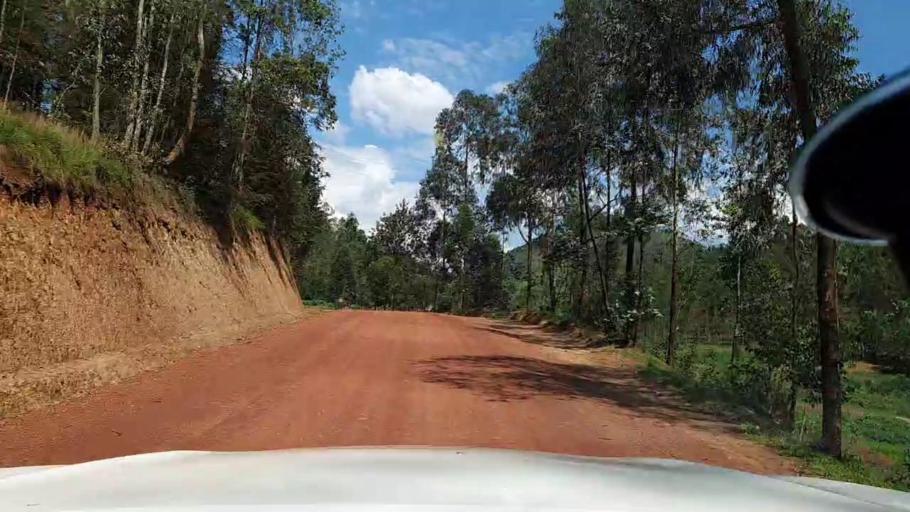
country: RW
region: Northern Province
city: Byumba
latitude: -1.7567
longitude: 29.8688
